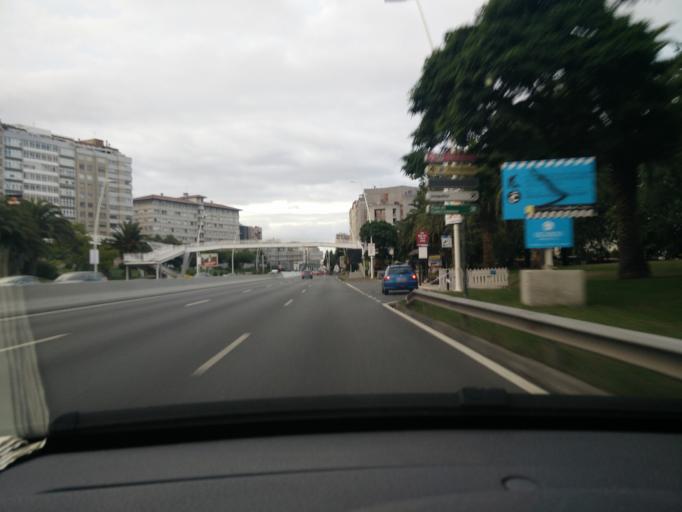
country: ES
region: Galicia
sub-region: Provincia da Coruna
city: A Coruna
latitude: 43.3527
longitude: -8.4068
